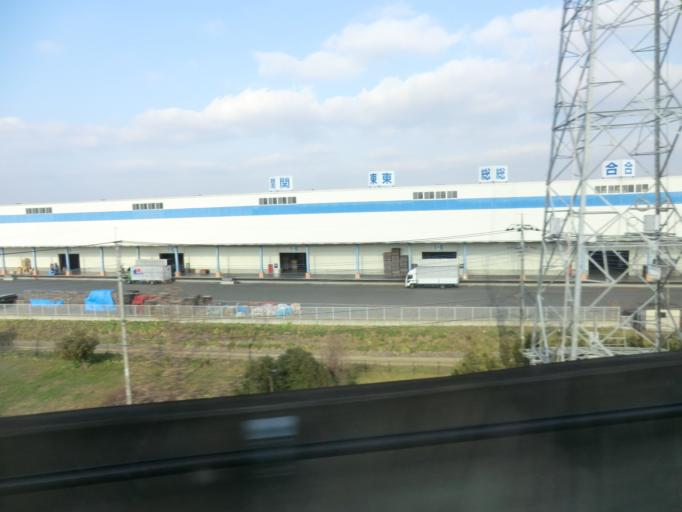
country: JP
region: Saitama
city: Fukiage-fujimi
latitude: 36.0990
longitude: 139.4820
